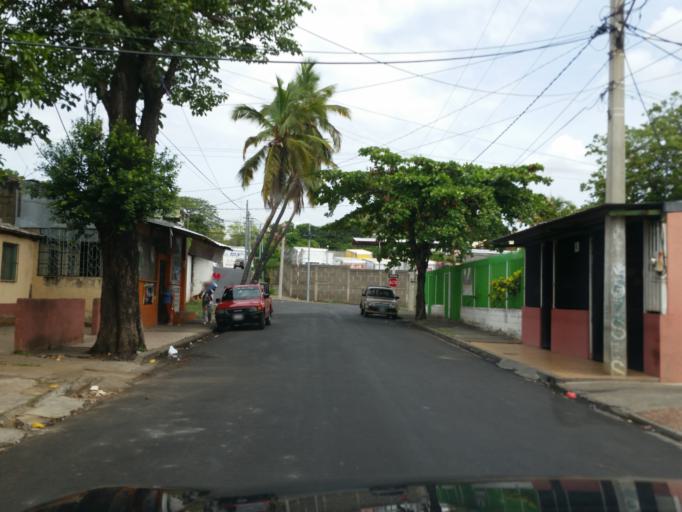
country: NI
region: Managua
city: Managua
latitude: 12.1411
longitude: -86.2665
